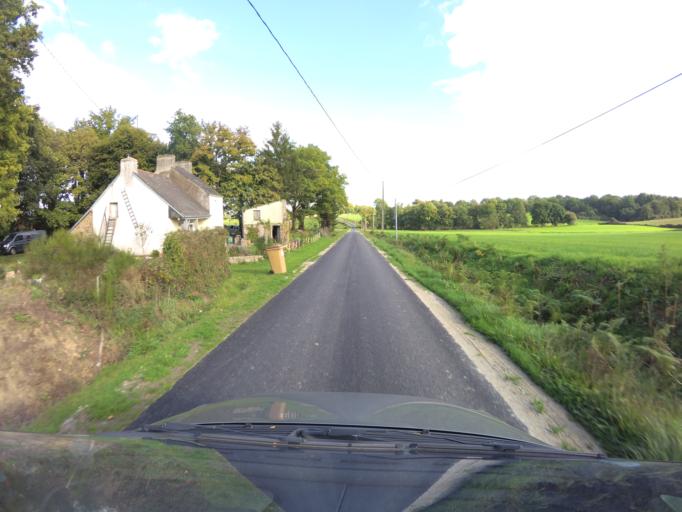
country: FR
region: Brittany
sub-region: Departement du Morbihan
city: Saint-Martin-sur-Oust
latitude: 47.7279
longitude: -2.2477
